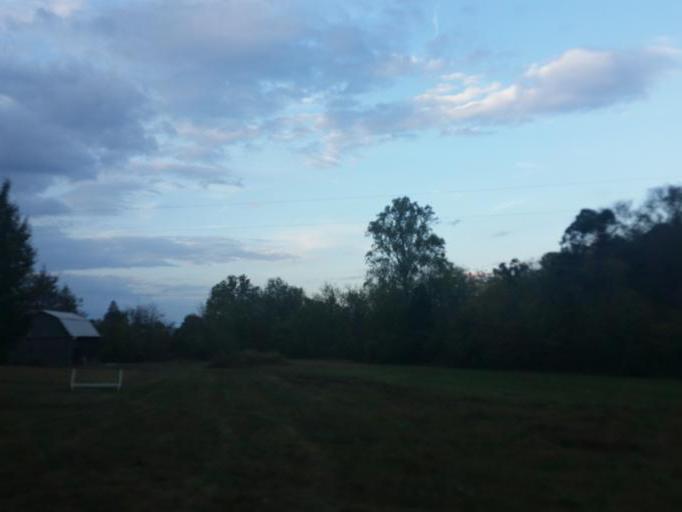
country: US
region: Tennessee
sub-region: Blount County
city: Louisville
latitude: 35.7870
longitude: -84.0656
